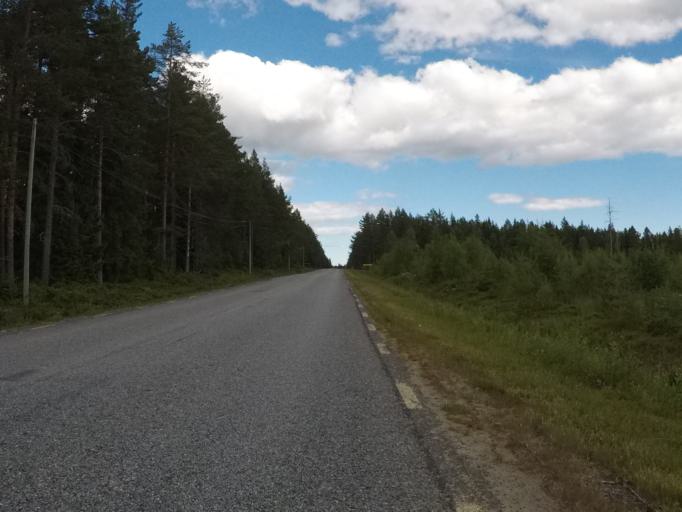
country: SE
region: Vaesterbotten
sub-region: Umea Kommun
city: Saevar
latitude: 63.9242
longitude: 20.7712
